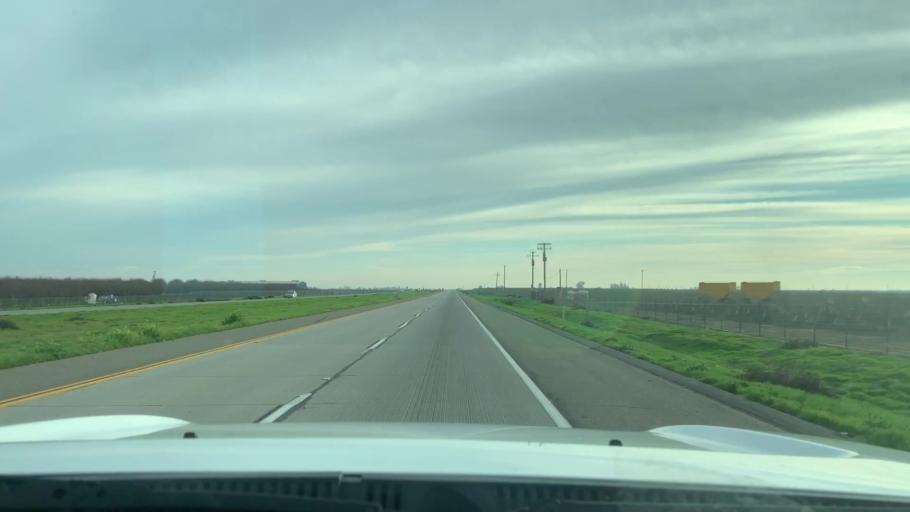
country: US
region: California
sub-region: Fresno County
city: Easton
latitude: 36.5865
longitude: -119.7862
